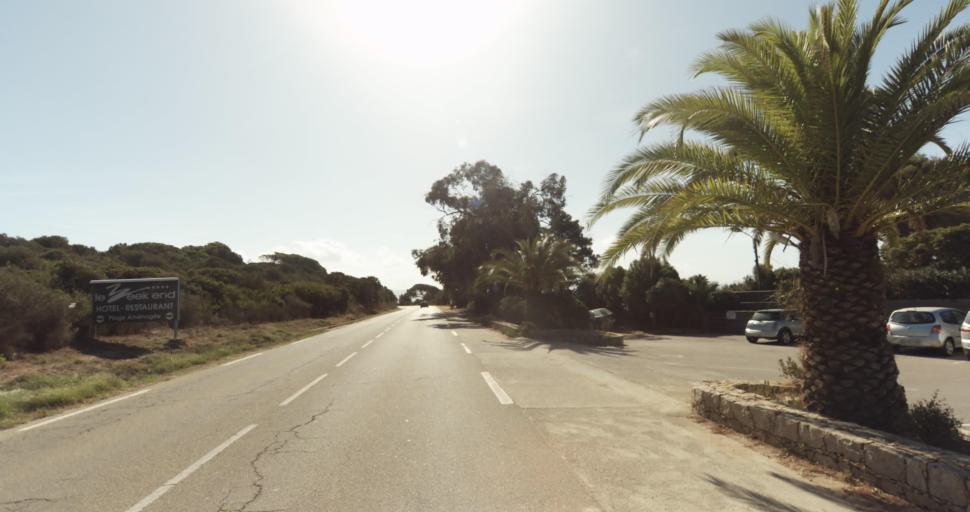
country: FR
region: Corsica
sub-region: Departement de la Corse-du-Sud
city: Ajaccio
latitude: 41.9103
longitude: 8.6481
